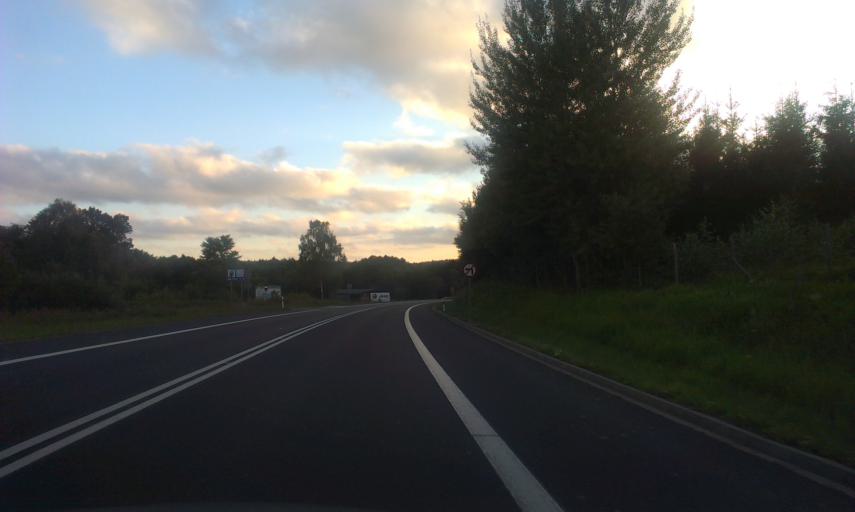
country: PL
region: West Pomeranian Voivodeship
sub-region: Powiat slawienski
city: Darlowo
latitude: 54.2796
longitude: 16.4841
